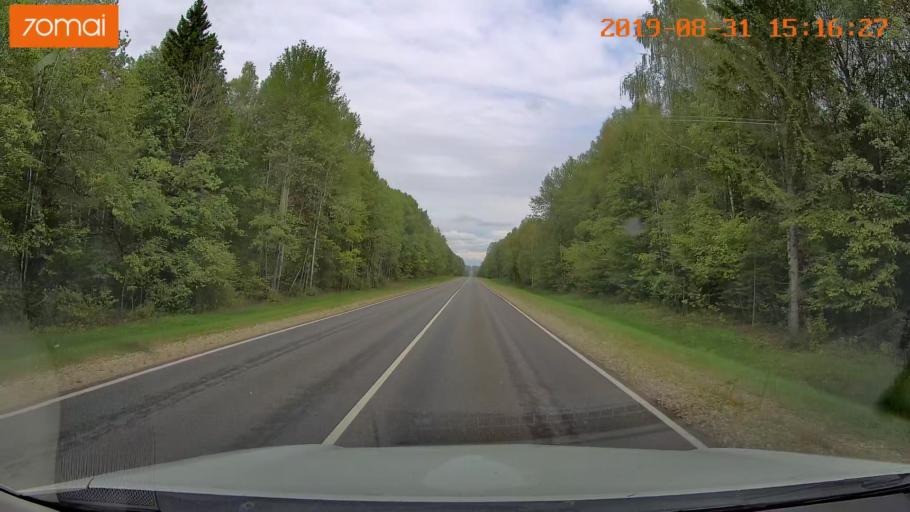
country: RU
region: Kaluga
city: Baryatino
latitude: 54.4600
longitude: 34.3505
